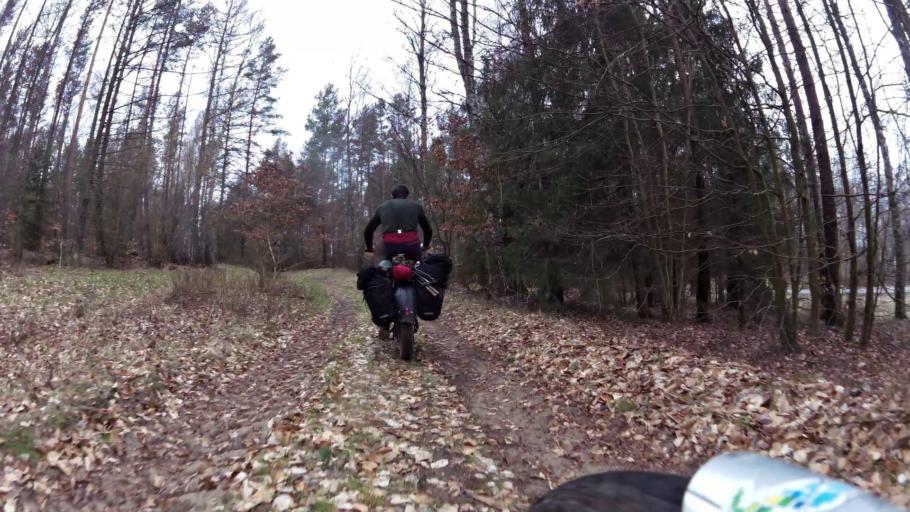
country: PL
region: Pomeranian Voivodeship
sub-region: Powiat bytowski
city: Trzebielino
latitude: 54.0856
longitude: 17.1254
